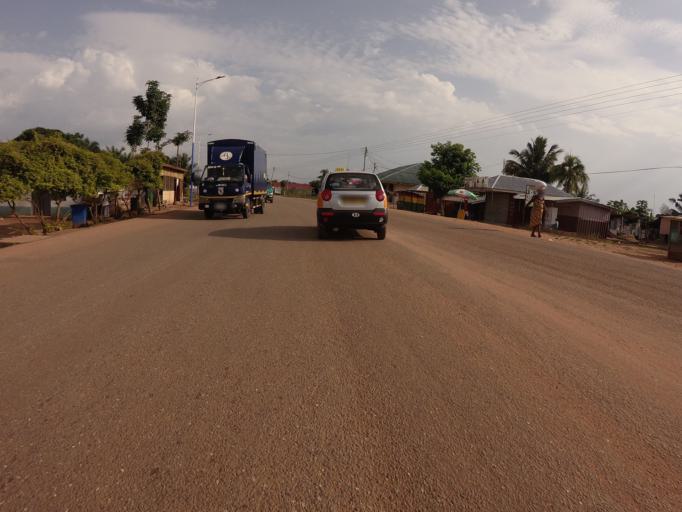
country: GH
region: Volta
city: Hohoe
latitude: 7.1410
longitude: 0.4630
